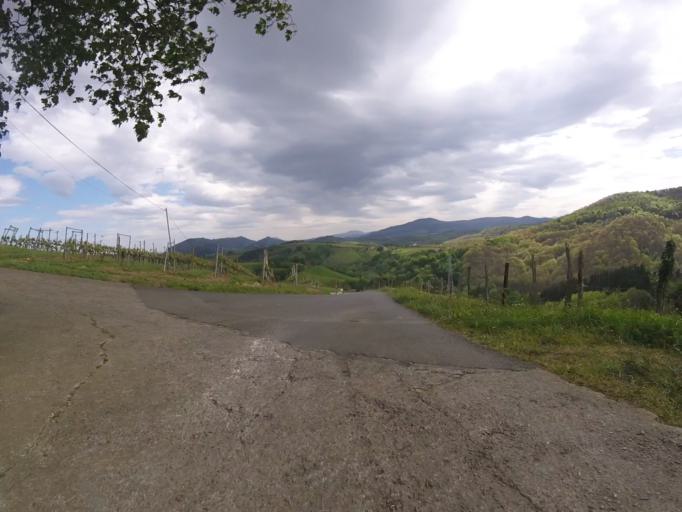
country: ES
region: Basque Country
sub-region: Provincia de Guipuzcoa
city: Zarautz
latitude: 43.2584
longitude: -2.1733
